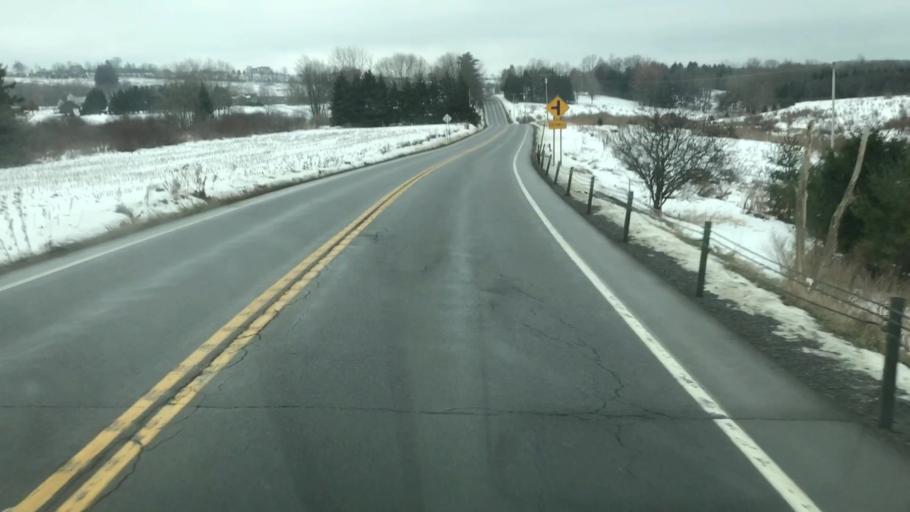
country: US
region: New York
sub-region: Cortland County
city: Cortland West
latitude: 42.6427
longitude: -76.2390
